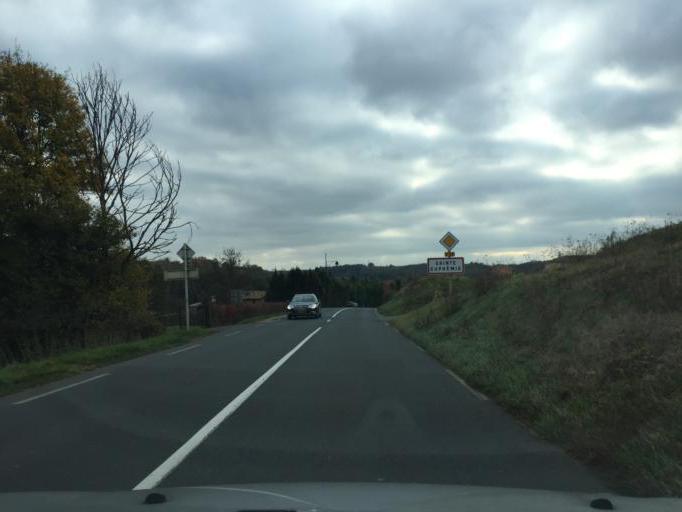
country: FR
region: Rhone-Alpes
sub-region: Departement de l'Ain
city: Sainte-Euphemie
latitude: 45.9763
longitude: 4.7984
